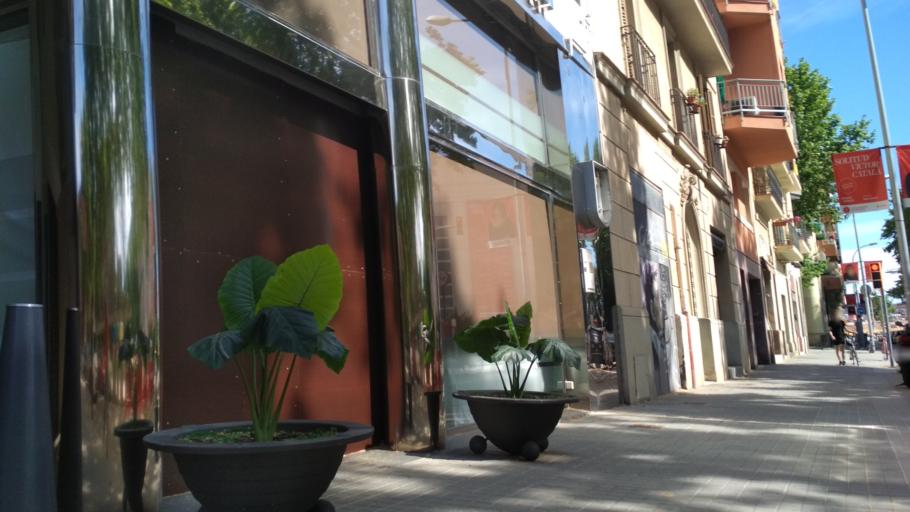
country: ES
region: Catalonia
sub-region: Provincia de Barcelona
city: Ciutat Vella
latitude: 41.4001
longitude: 2.1842
